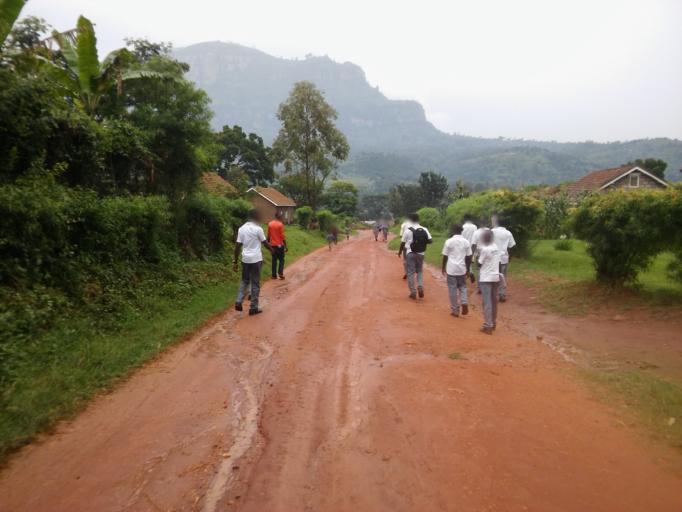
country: UG
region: Eastern Region
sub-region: Bududa District
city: Bududa
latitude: 0.9870
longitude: 34.2265
